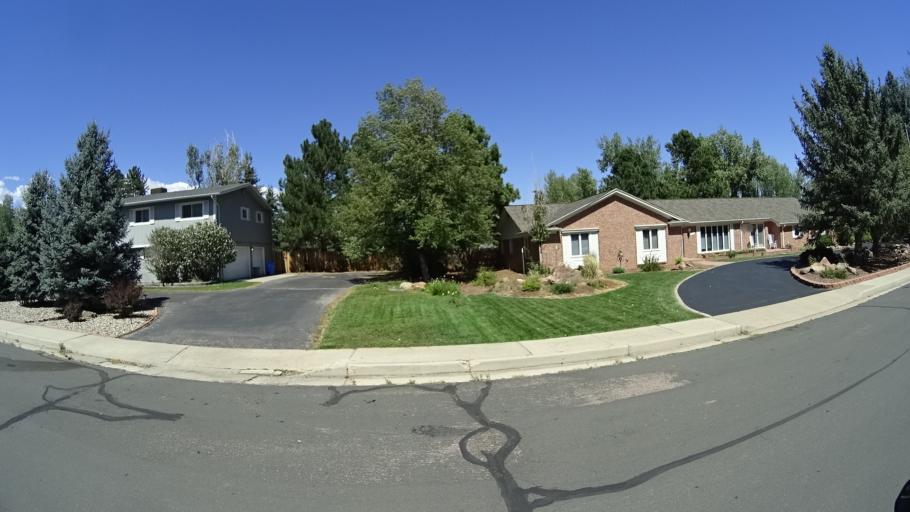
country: US
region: Colorado
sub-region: El Paso County
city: Colorado Springs
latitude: 38.7866
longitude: -104.8315
